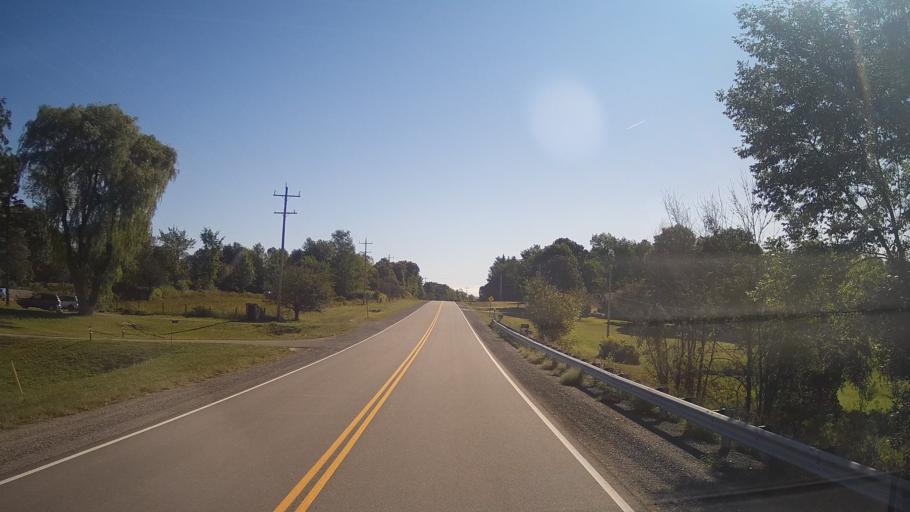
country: CA
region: Ontario
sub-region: Lanark County
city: Smiths Falls
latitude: 44.6252
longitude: -75.9892
